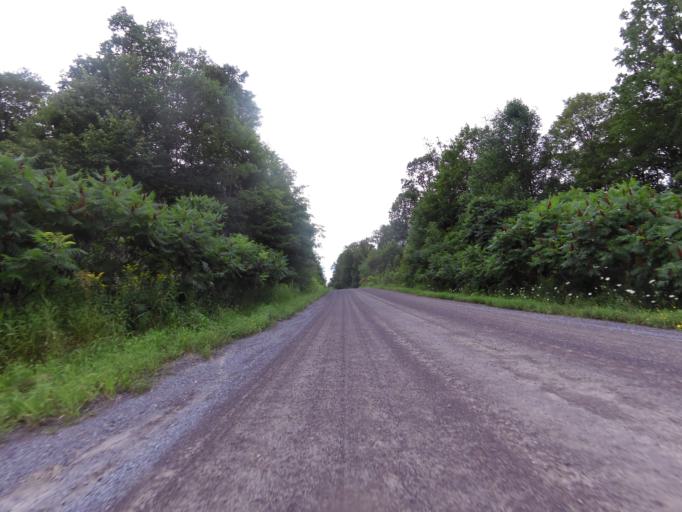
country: CA
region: Ontario
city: Carleton Place
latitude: 45.1646
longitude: -76.2733
